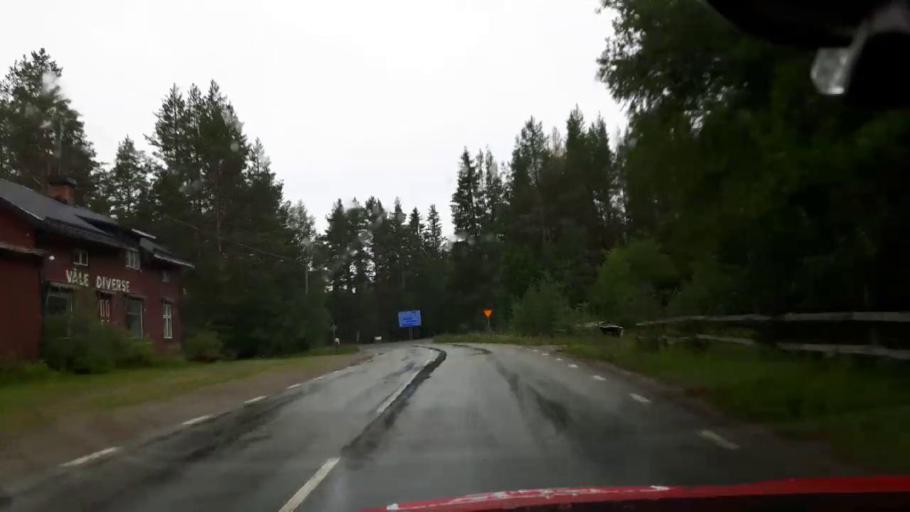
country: SE
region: Jaemtland
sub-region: OEstersunds Kommun
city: Brunflo
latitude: 62.7743
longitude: 15.0129
